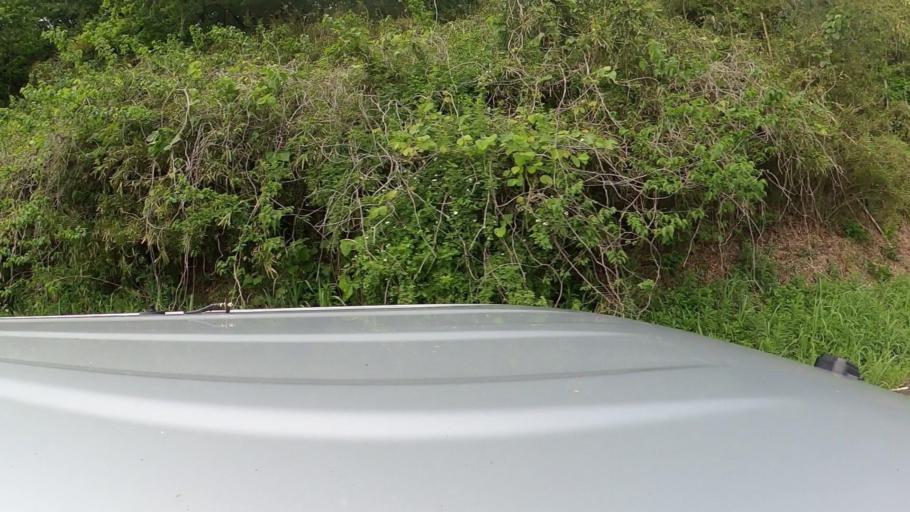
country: JP
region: Ibaraki
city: Ushiku
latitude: 35.9662
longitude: 140.1980
